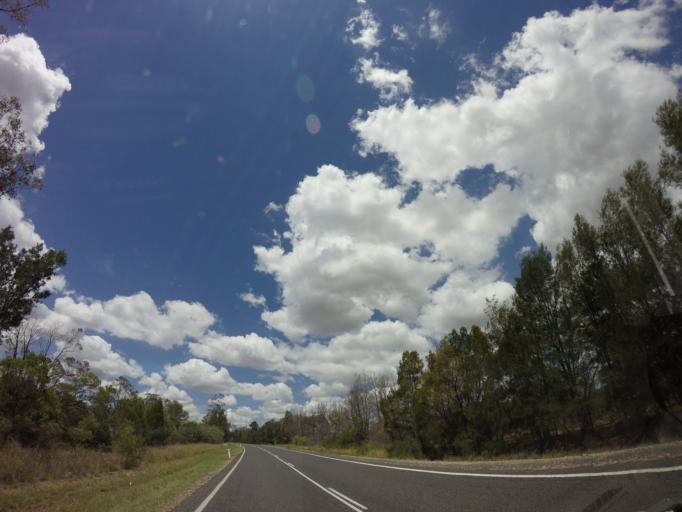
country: AU
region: Queensland
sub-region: Toowoomba
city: Oakey
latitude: -27.9515
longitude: 151.1393
